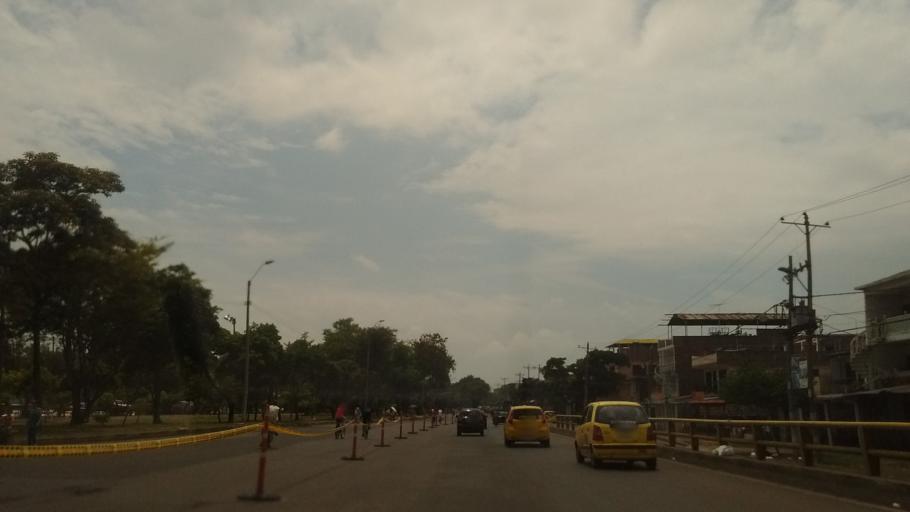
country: CO
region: Valle del Cauca
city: Cali
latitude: 3.4650
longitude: -76.4845
